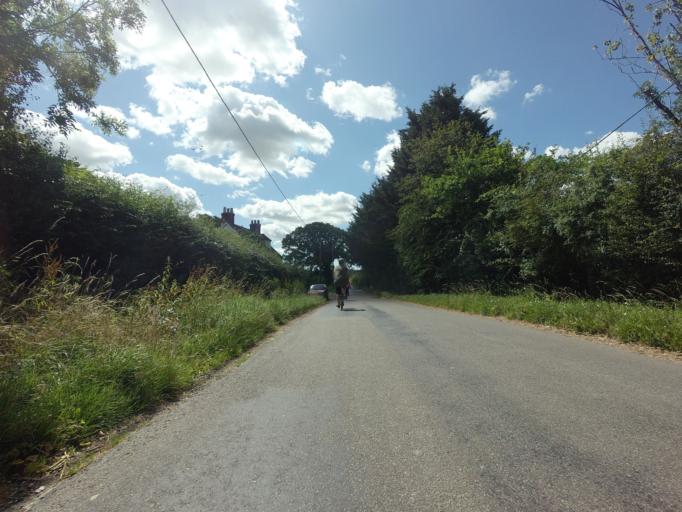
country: GB
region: England
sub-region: East Sussex
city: Hailsham
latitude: 50.8863
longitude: 0.1855
